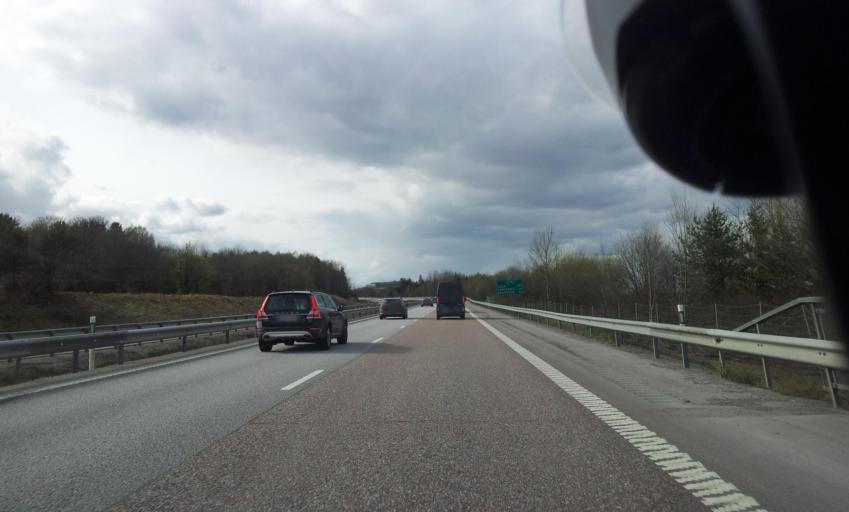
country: SE
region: Uppsala
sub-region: Habo Kommun
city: Balsta
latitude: 59.5880
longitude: 17.5029
